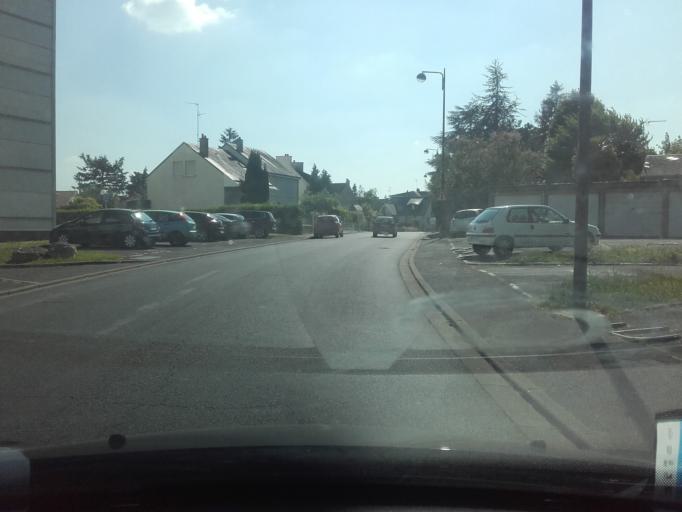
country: FR
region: Centre
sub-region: Departement d'Indre-et-Loire
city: Saint-Cyr-sur-Loire
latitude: 47.4111
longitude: 0.6748
